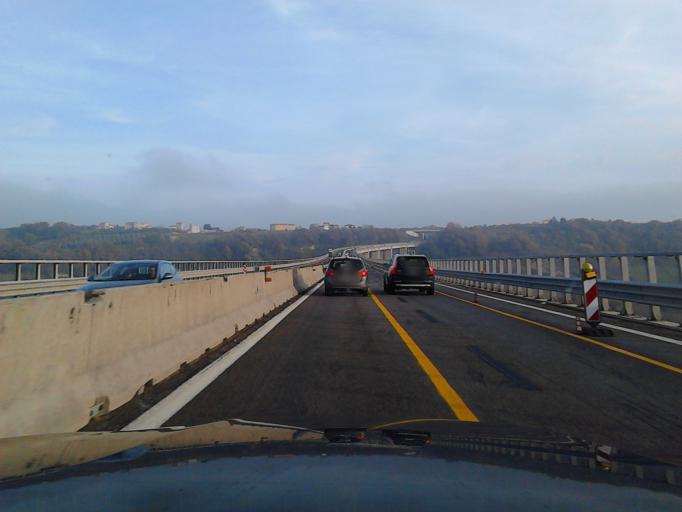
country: IT
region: Abruzzo
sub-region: Provincia di Chieti
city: Ortona
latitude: 42.3138
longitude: 14.4114
